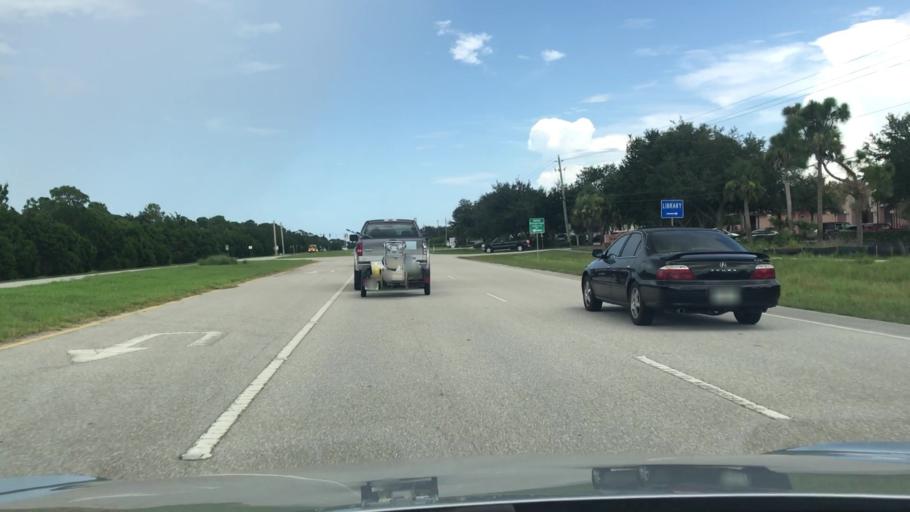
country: US
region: Florida
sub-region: Indian River County
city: Sebastian
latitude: 27.7776
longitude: -80.4986
